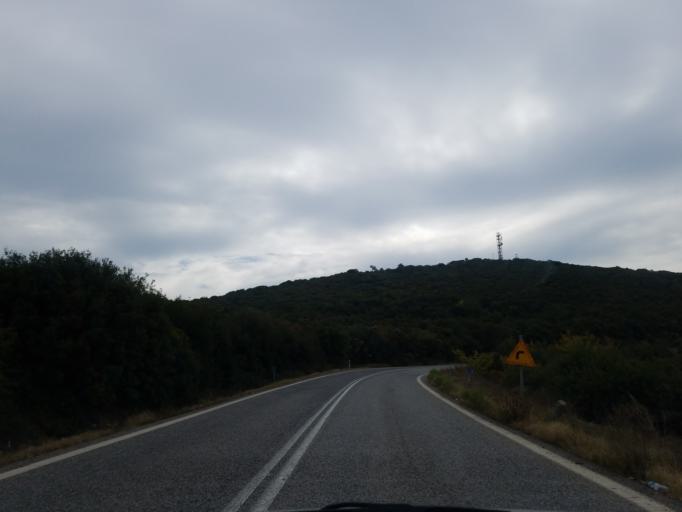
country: GR
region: Central Greece
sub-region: Nomos Fthiotidos
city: Domokos
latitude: 39.1384
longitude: 22.3101
